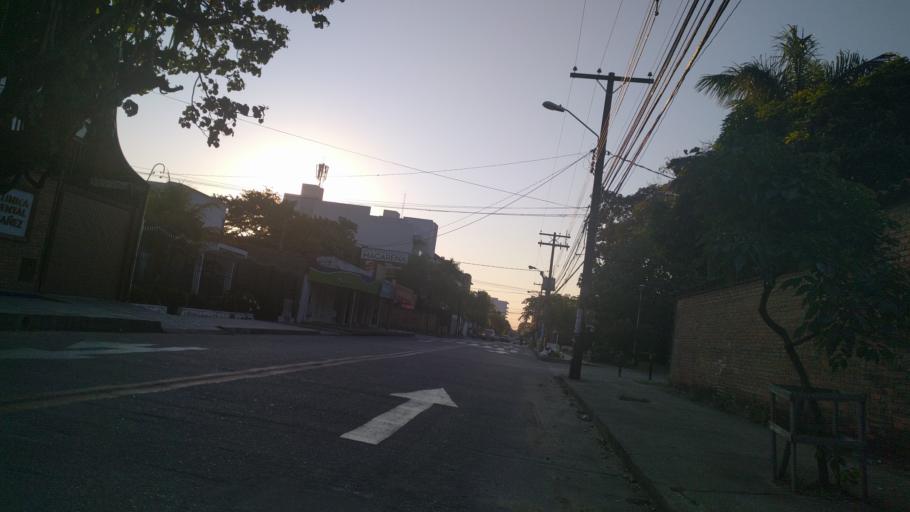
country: BO
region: Santa Cruz
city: Santa Cruz de la Sierra
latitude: -17.8068
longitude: -63.2066
